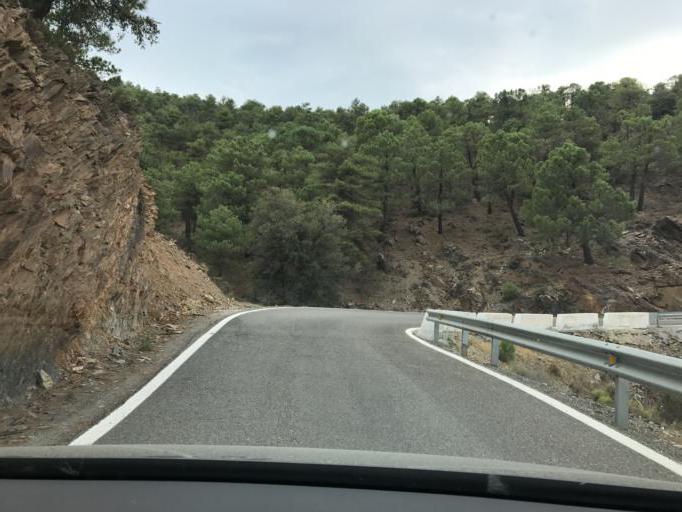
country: ES
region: Andalusia
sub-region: Provincia de Granada
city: Aldeire
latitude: 37.1617
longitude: -3.0523
